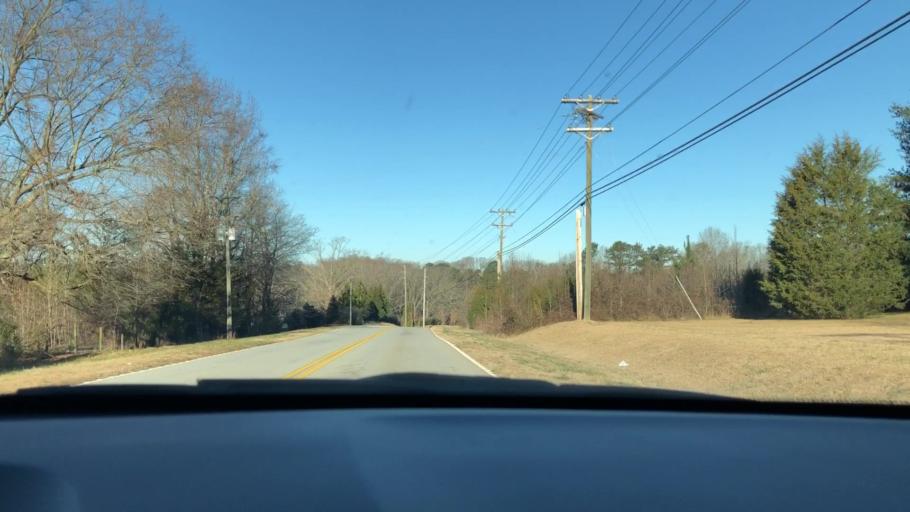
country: US
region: South Carolina
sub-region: Greenville County
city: Five Forks
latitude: 34.8227
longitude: -82.2134
